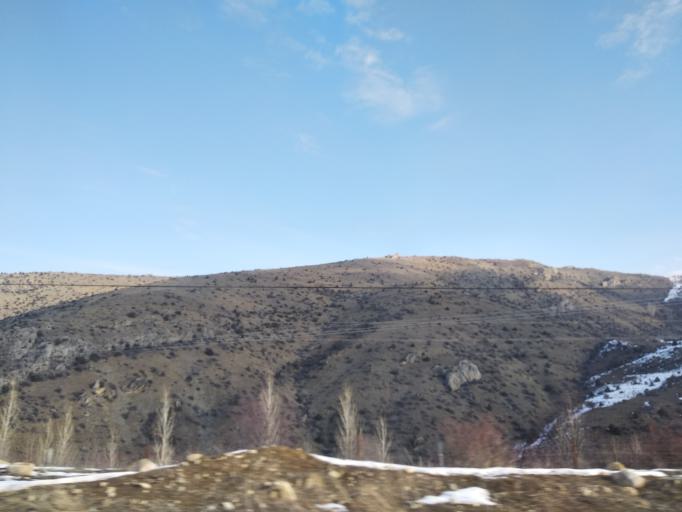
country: TR
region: Gumushane
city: Kelkit
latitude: 40.0861
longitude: 39.4811
